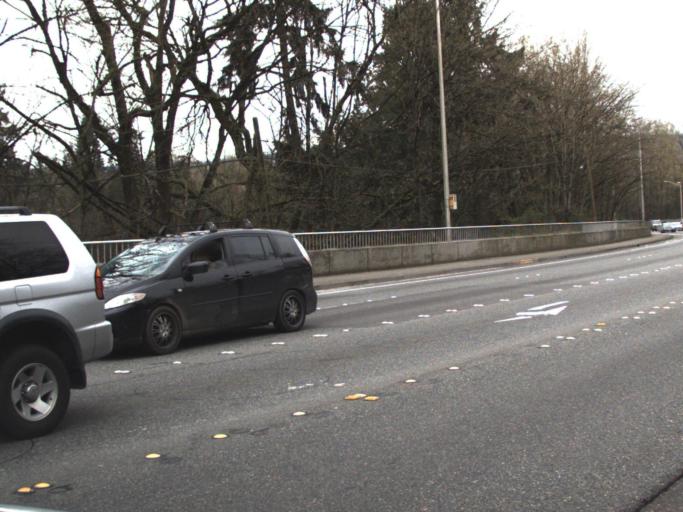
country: US
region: Washington
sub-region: King County
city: Kent
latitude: 47.3788
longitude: -122.2159
